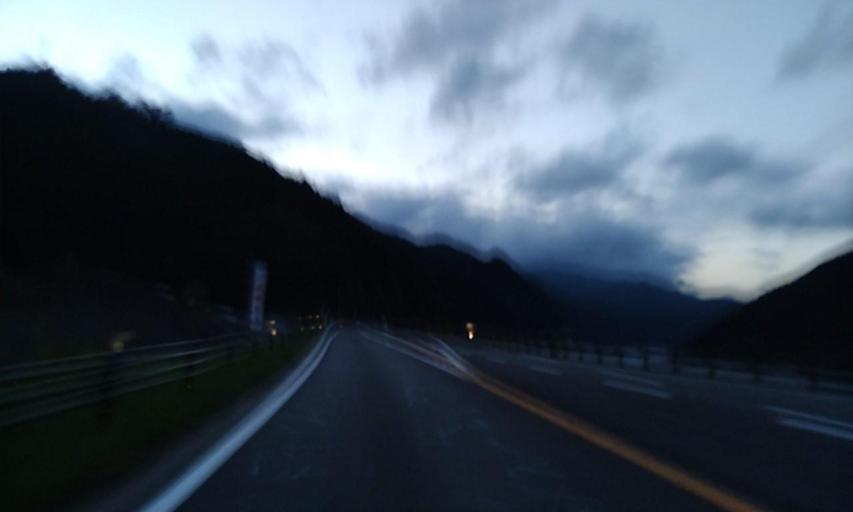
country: JP
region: Wakayama
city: Shingu
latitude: 33.7248
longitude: 135.9598
